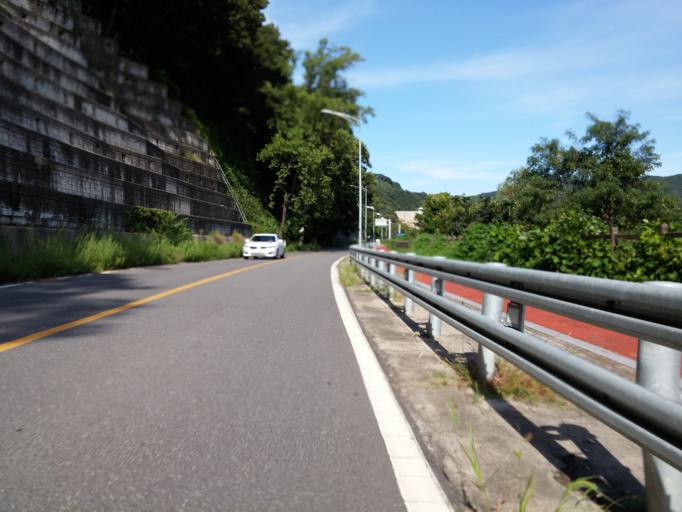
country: KR
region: Daejeon
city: Sintansin
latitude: 36.4760
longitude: 127.4719
